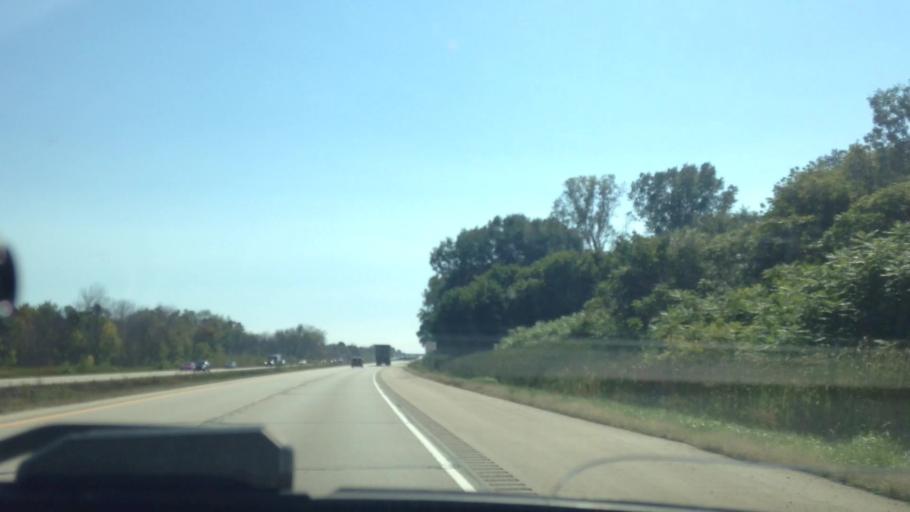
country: US
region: Wisconsin
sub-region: Ozaukee County
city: Grafton
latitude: 43.2722
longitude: -87.9202
